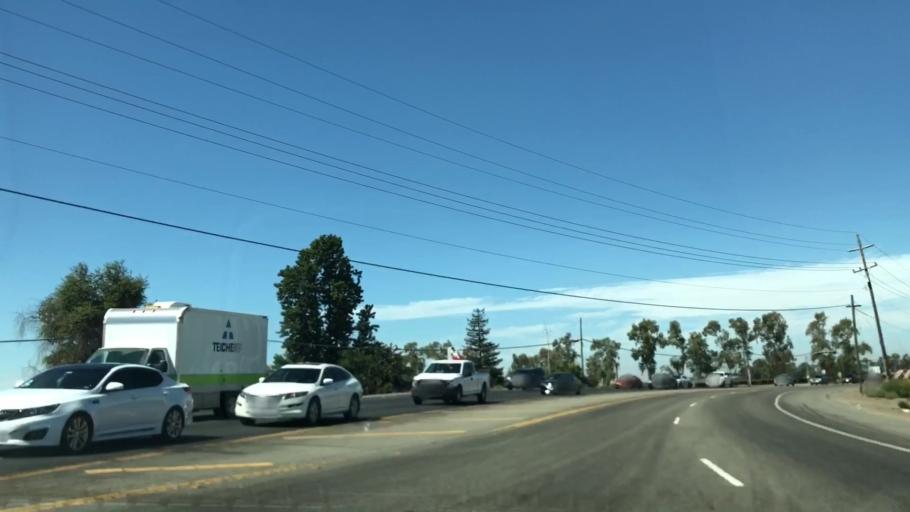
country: US
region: California
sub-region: Contra Costa County
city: Byron
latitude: 37.8906
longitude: -121.6410
